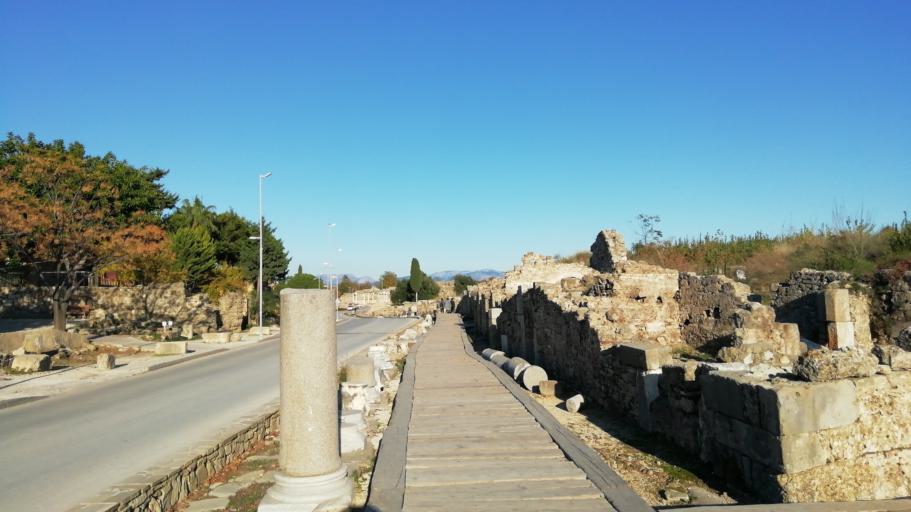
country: TR
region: Antalya
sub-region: Manavgat
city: Side
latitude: 36.7691
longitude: 31.3918
